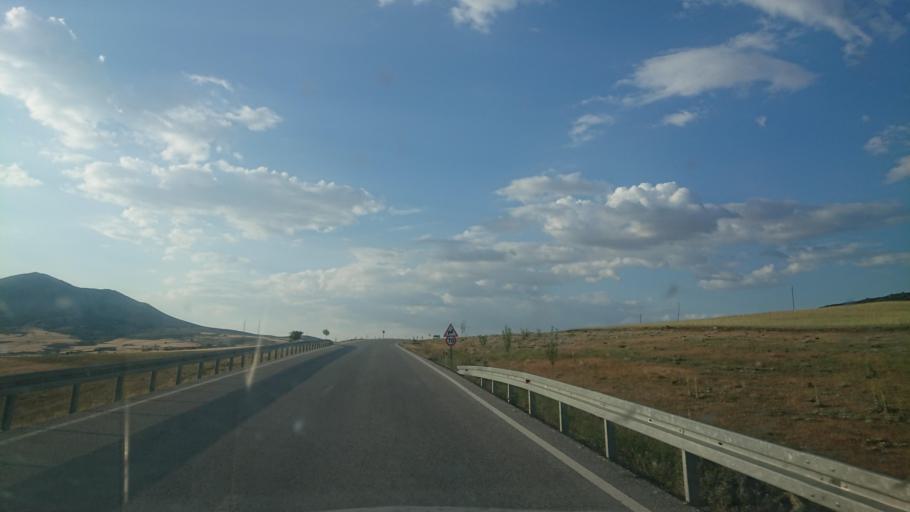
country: TR
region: Aksaray
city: Balci
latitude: 38.5955
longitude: 34.1016
